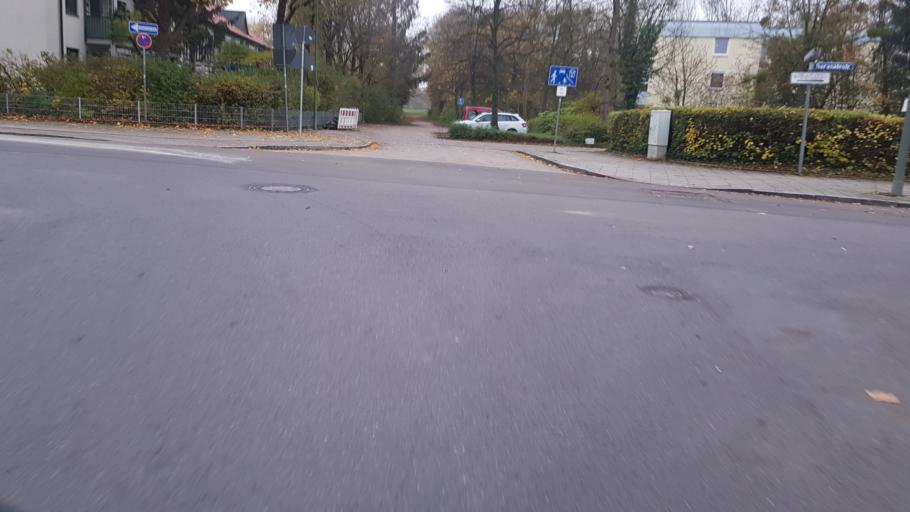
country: DE
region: Bavaria
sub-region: Upper Bavaria
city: Pasing
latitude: 48.1625
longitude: 11.4767
